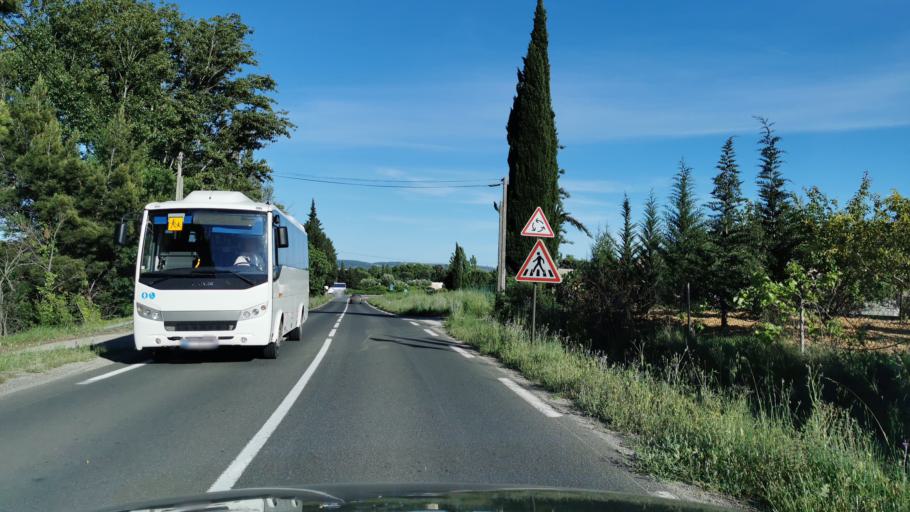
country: FR
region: Languedoc-Roussillon
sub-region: Departement de l'Aude
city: Narbonne
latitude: 43.1992
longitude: 2.9712
